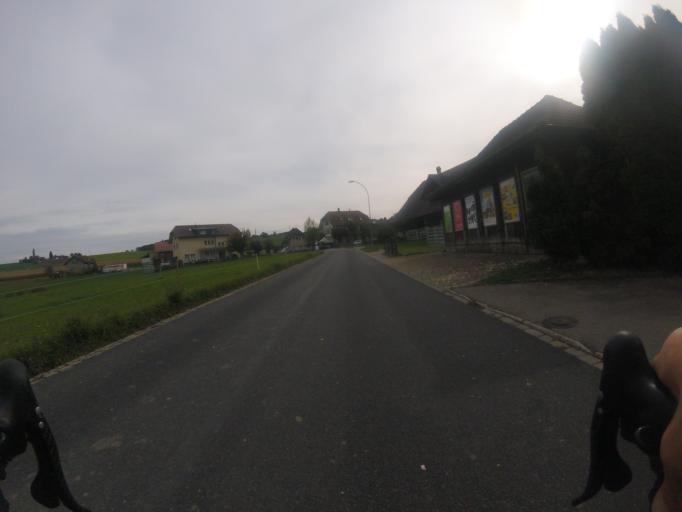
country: CH
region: Bern
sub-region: Bern-Mittelland District
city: Frauenkappelen
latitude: 46.9409
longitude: 7.3362
